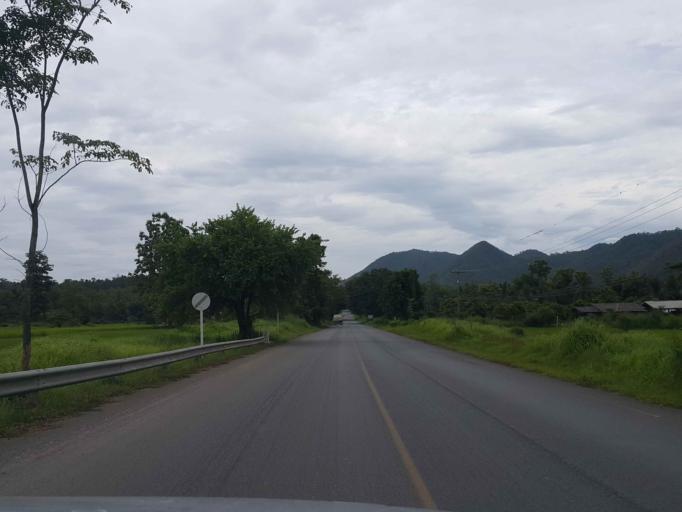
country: TH
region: Lampang
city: Thoen
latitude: 17.5436
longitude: 99.3380
